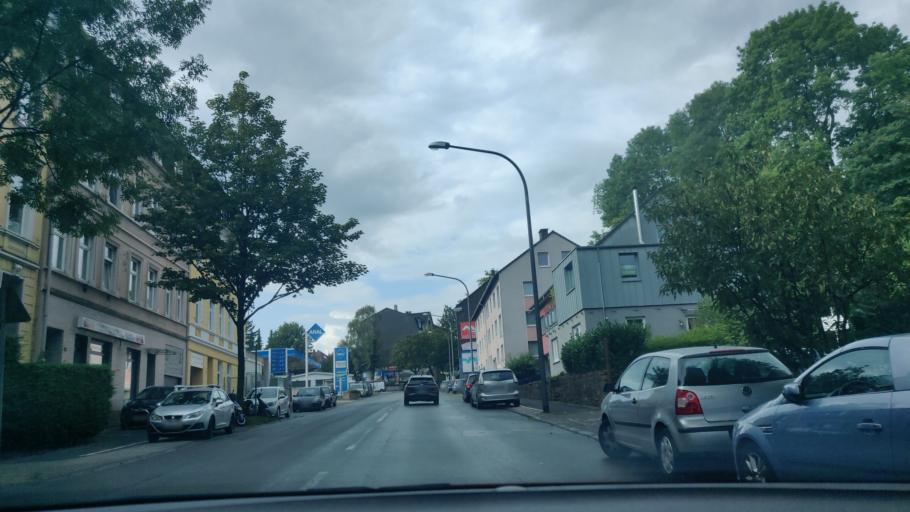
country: DE
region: North Rhine-Westphalia
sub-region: Regierungsbezirk Dusseldorf
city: Wuppertal
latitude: 51.2683
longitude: 7.1280
